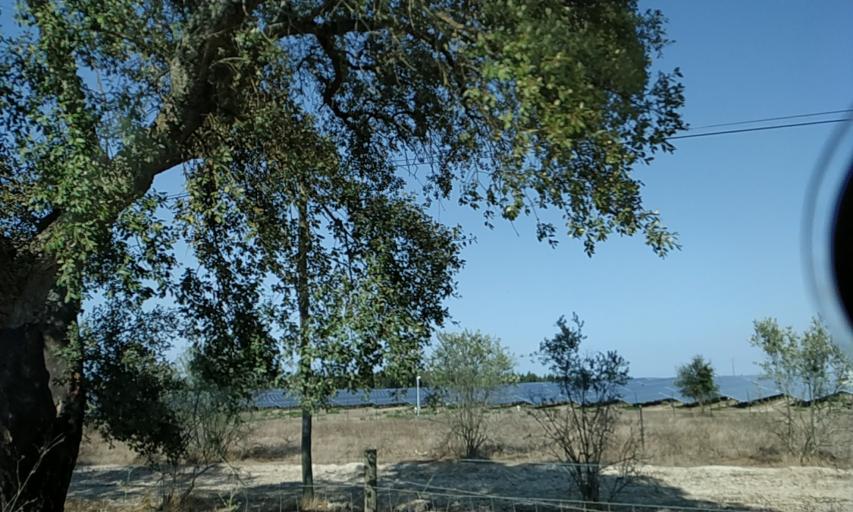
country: PT
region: Evora
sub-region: Vendas Novas
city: Vendas Novas
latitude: 38.7238
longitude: -8.6205
